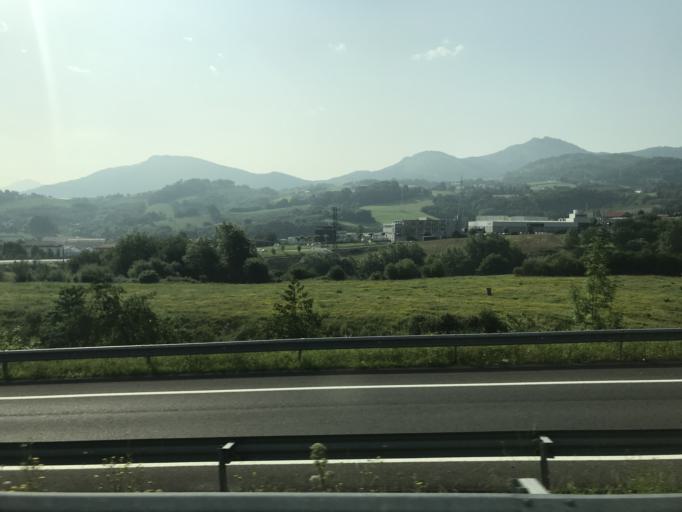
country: ES
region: Basque Country
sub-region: Provincia de Guipuzcoa
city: Urnieta
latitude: 43.2419
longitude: -2.0002
